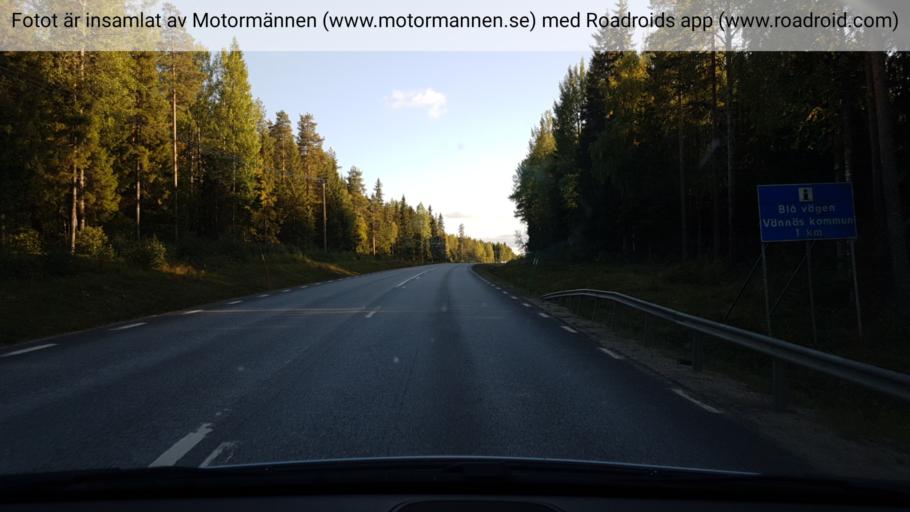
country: SE
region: Vaesterbotten
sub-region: Vannas Kommun
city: Vaennaes
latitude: 63.9402
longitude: 19.7714
